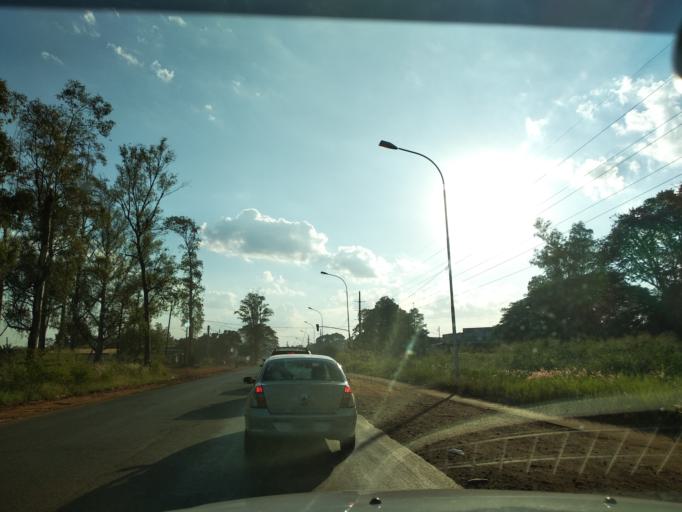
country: AR
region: Misiones
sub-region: Departamento de Capital
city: Posadas
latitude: -27.4292
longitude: -55.9380
